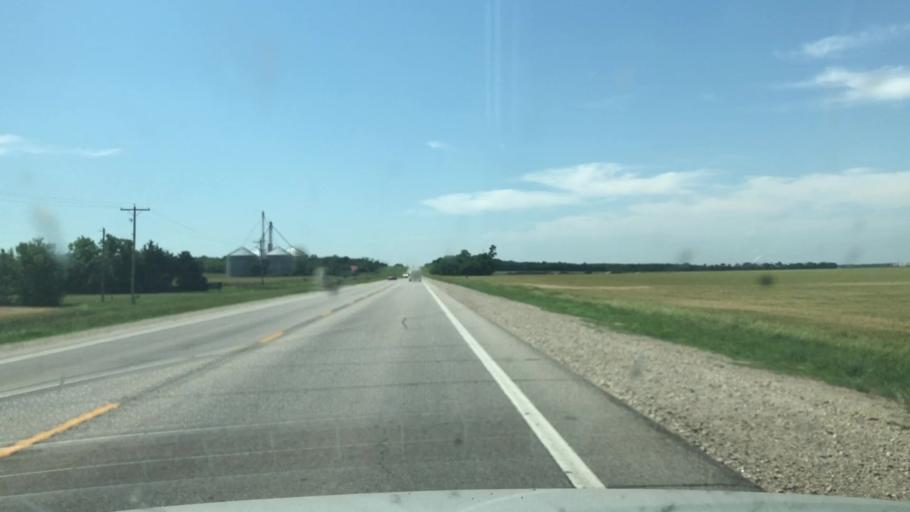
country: US
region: Kansas
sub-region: Butler County
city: Douglass
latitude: 37.3828
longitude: -97.0069
